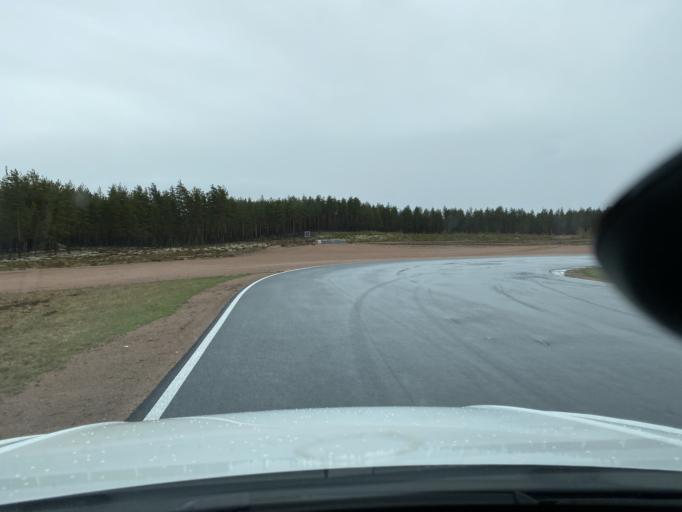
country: FI
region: Satakunta
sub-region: Pori
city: Vampula
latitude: 60.9766
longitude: 22.6708
